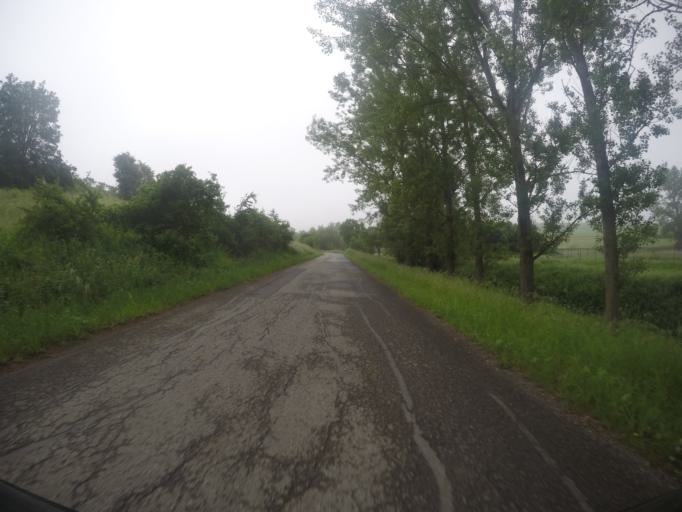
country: DE
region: Bavaria
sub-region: Regierungsbezirk Unterfranken
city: Schwanfeld
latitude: 49.9181
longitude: 10.1513
